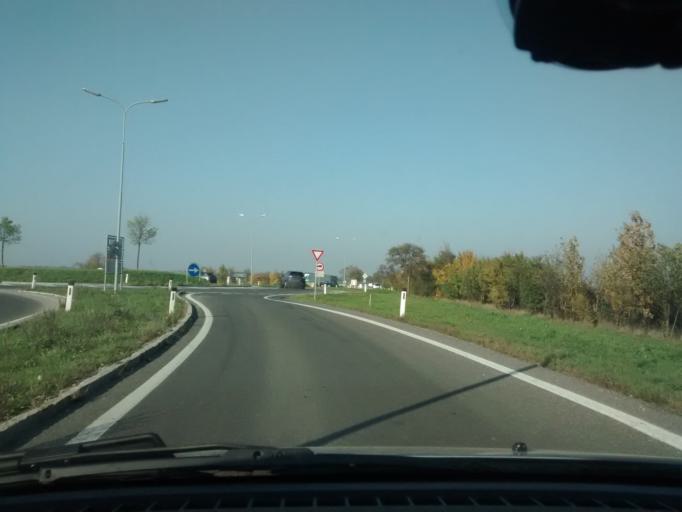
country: AT
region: Lower Austria
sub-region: Politischer Bezirk Modling
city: Munchendorf
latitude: 48.0450
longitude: 16.3821
